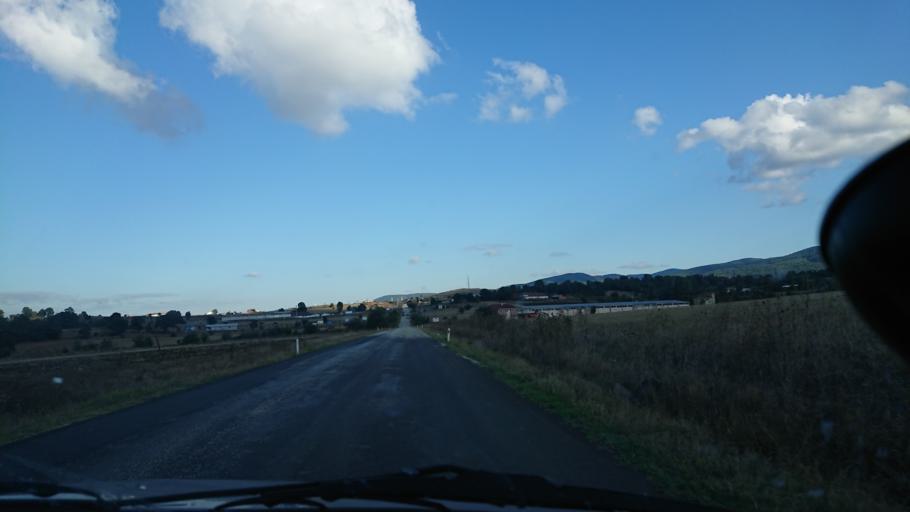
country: TR
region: Bilecik
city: Pazaryeri
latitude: 40.0057
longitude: 29.8766
